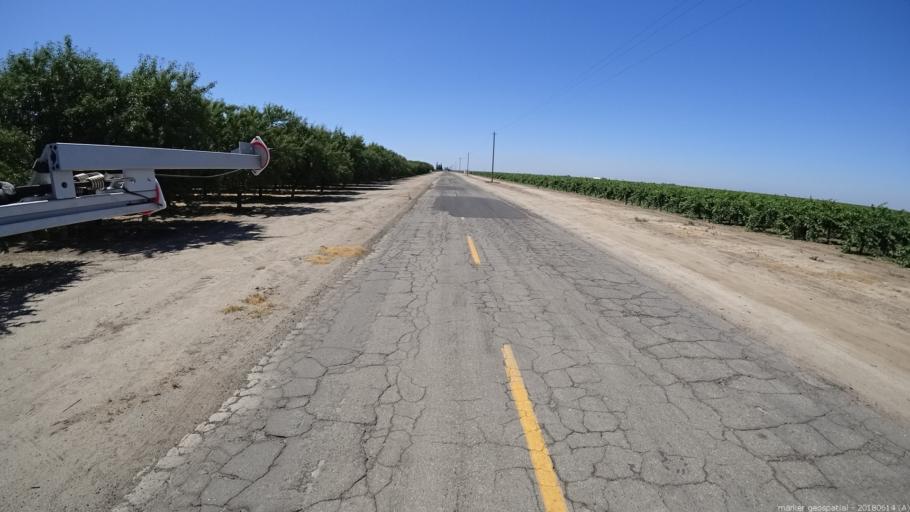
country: US
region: California
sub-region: Madera County
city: Fairmead
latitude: 36.9769
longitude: -120.1842
